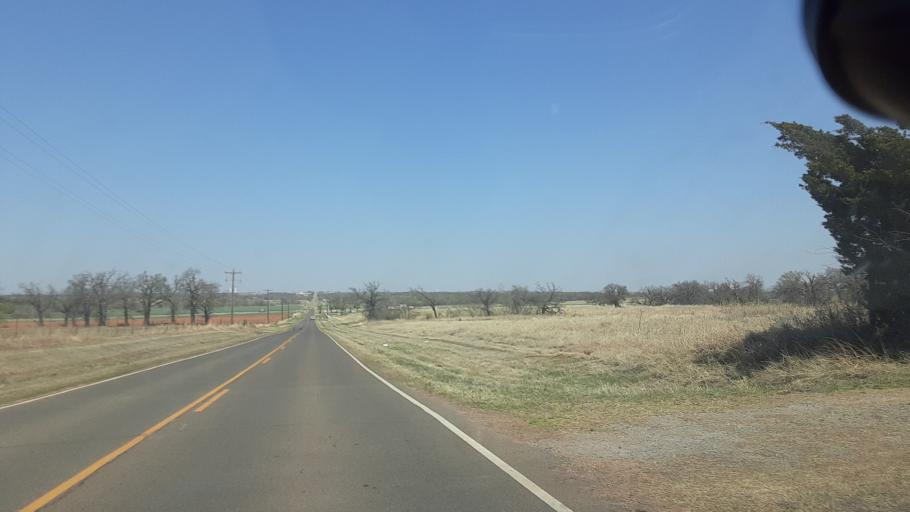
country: US
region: Oklahoma
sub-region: Logan County
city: Guthrie
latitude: 35.7996
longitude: -97.4783
